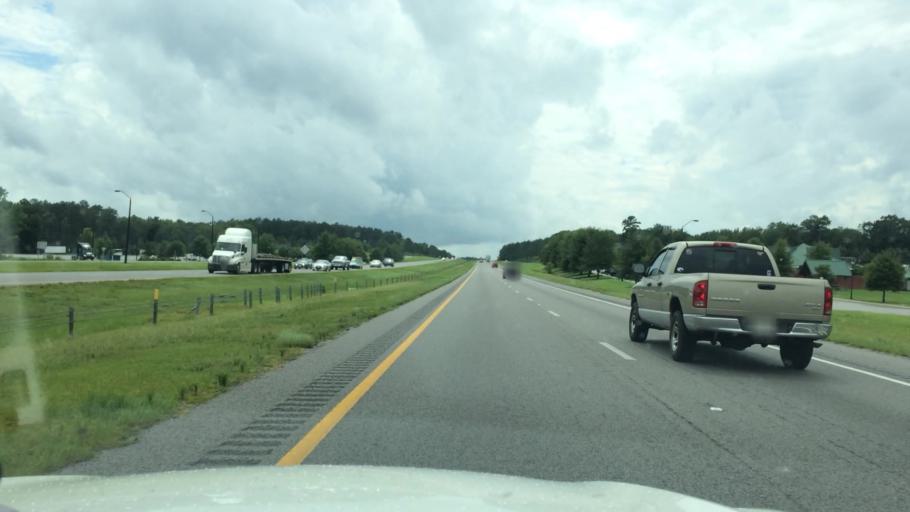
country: US
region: South Carolina
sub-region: Kershaw County
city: Lugoff
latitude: 34.2020
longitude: -80.6592
